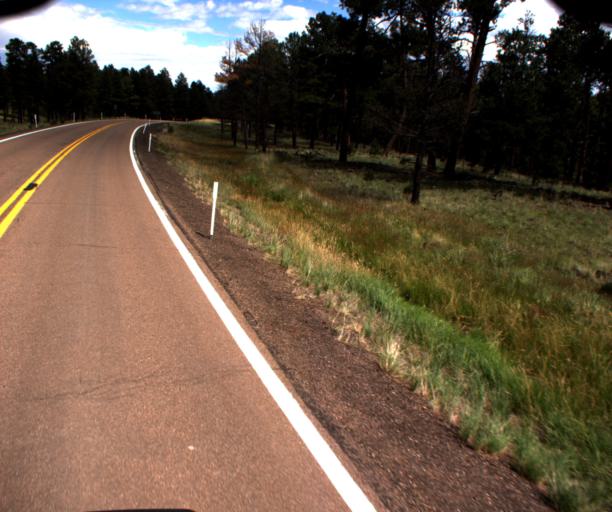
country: US
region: Arizona
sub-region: Apache County
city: Eagar
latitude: 34.0766
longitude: -109.4757
